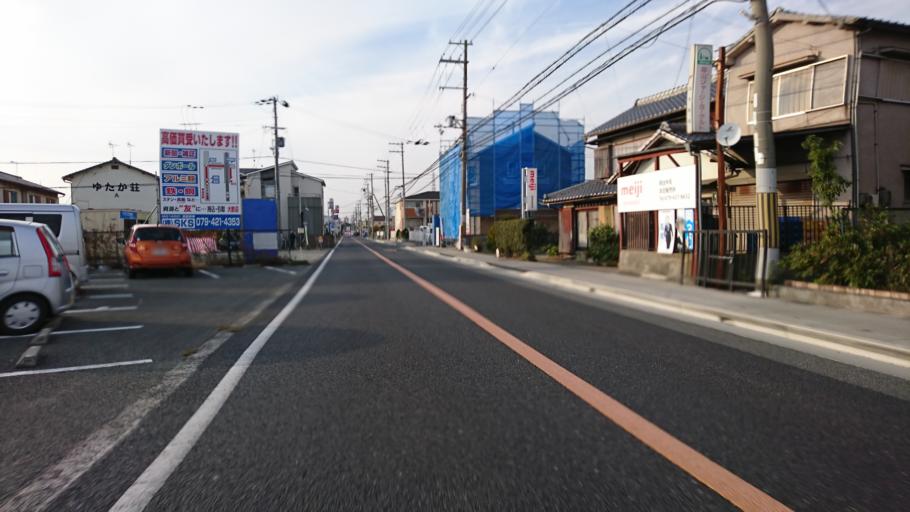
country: JP
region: Hyogo
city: Kakogawacho-honmachi
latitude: 34.7172
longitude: 134.8590
